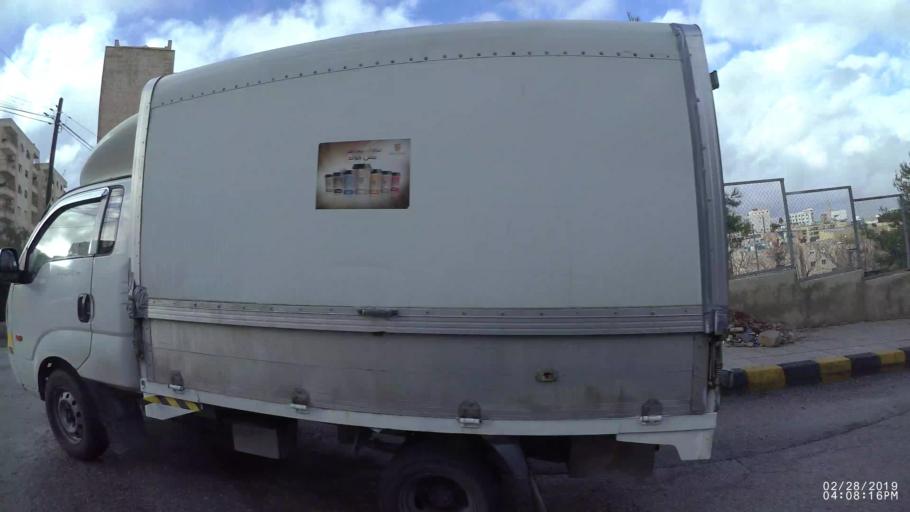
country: JO
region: Amman
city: Amman
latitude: 31.9999
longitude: 35.9249
